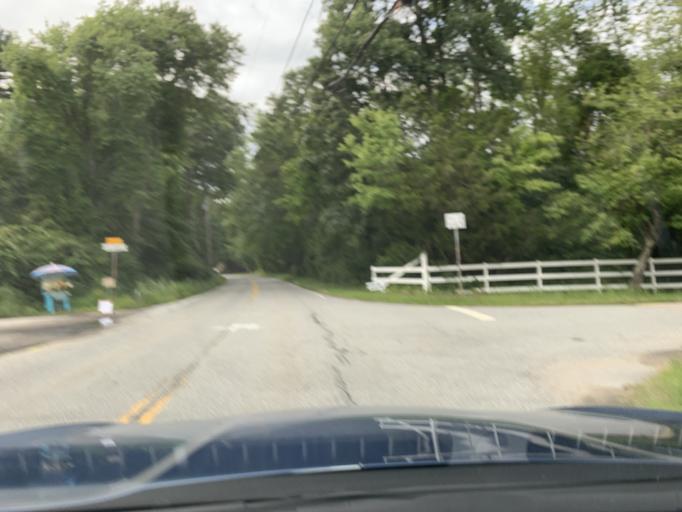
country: US
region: Rhode Island
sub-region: Kent County
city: East Greenwich
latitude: 41.6232
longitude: -71.4465
